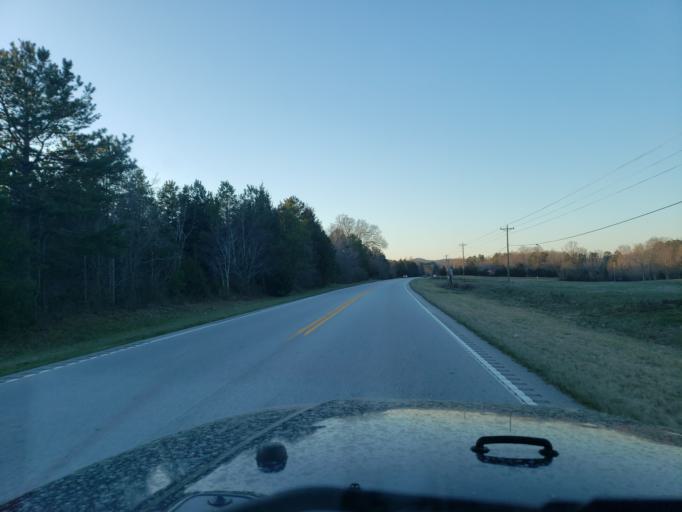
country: US
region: South Carolina
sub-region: York County
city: Clover
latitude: 35.1450
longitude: -81.3167
